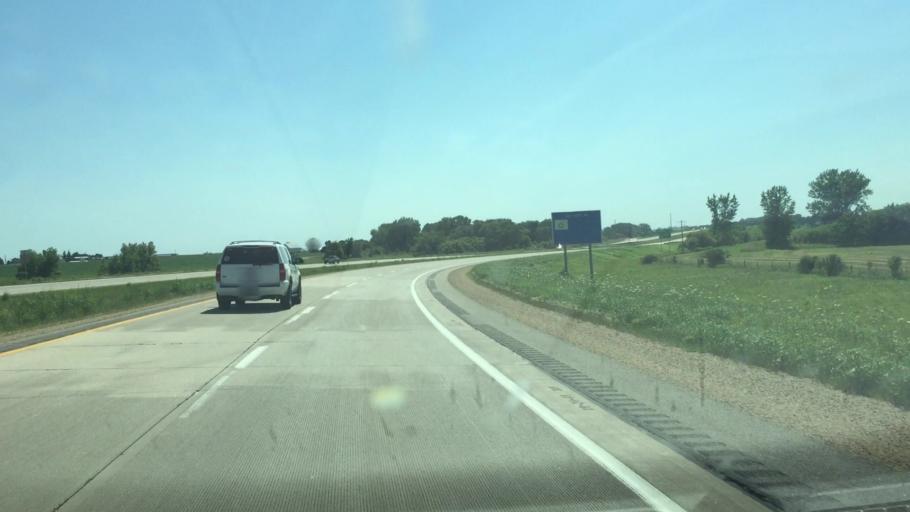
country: US
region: Iowa
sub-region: Jones County
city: Monticello
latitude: 42.2092
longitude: -91.1770
